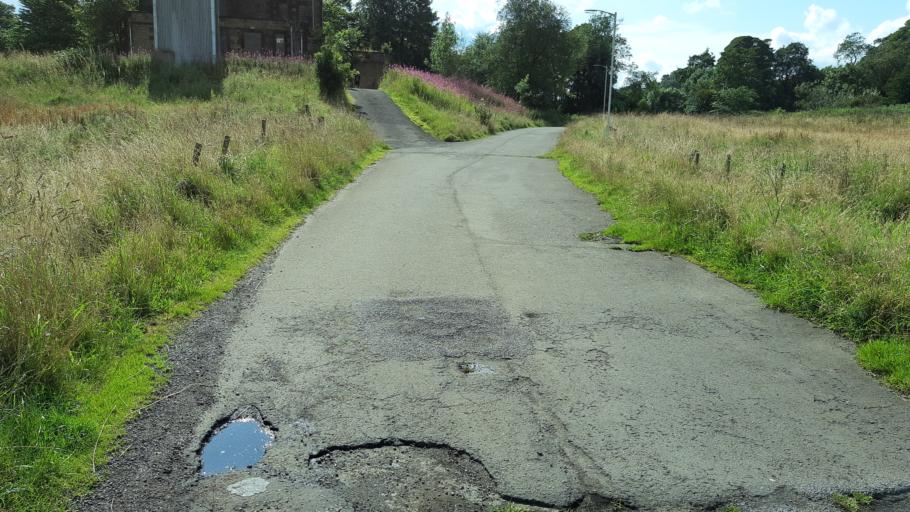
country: GB
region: Scotland
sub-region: West Lothian
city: Livingston
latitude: 55.9178
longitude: -3.5581
